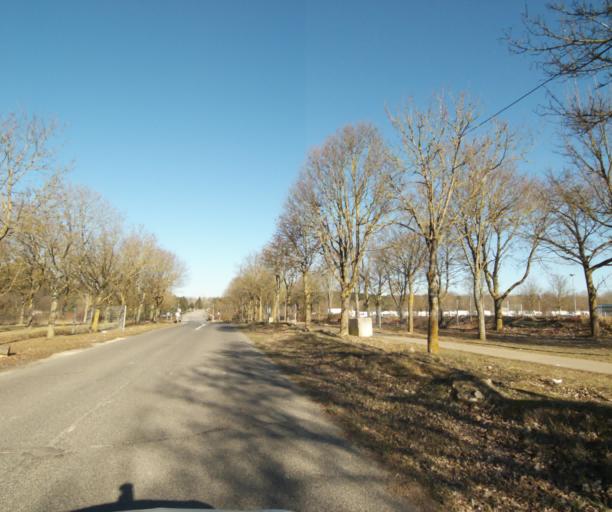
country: FR
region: Lorraine
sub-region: Departement de Meurthe-et-Moselle
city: Maxeville
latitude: 48.7092
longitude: 6.1488
